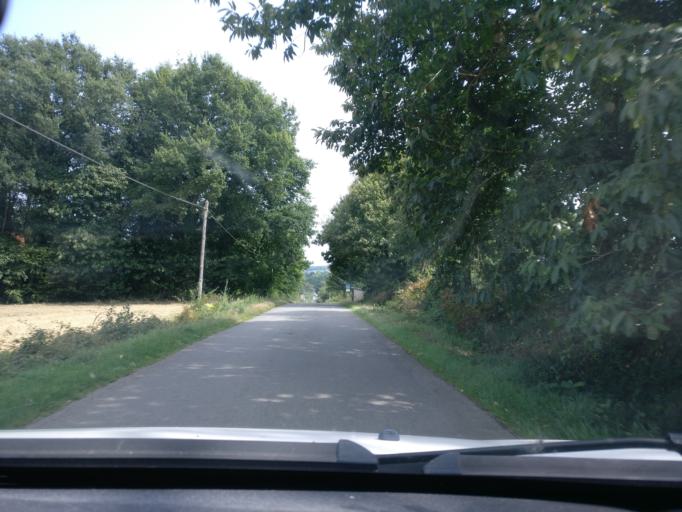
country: FR
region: Brittany
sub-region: Departement d'Ille-et-Vilaine
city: Erce-pres-Liffre
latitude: 48.2623
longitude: -1.5253
